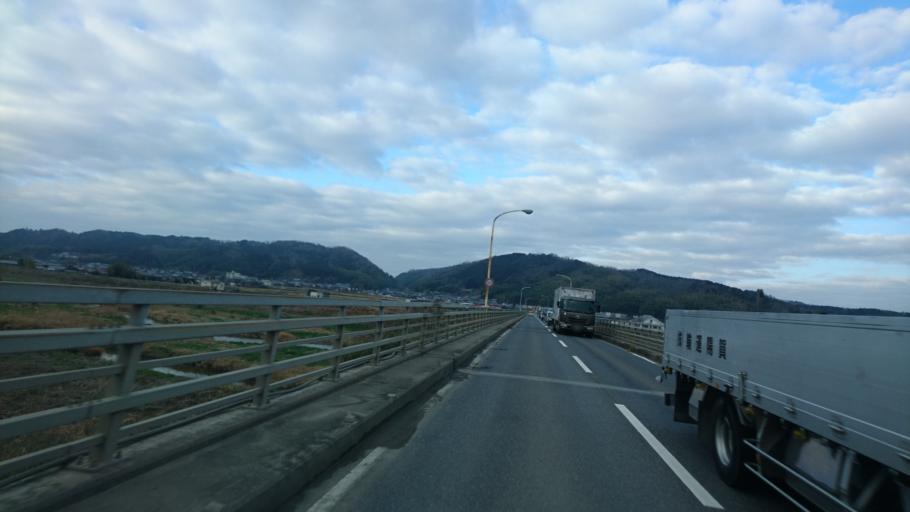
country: JP
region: Mie
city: Ueno-ebisumachi
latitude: 34.7730
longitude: 136.1124
